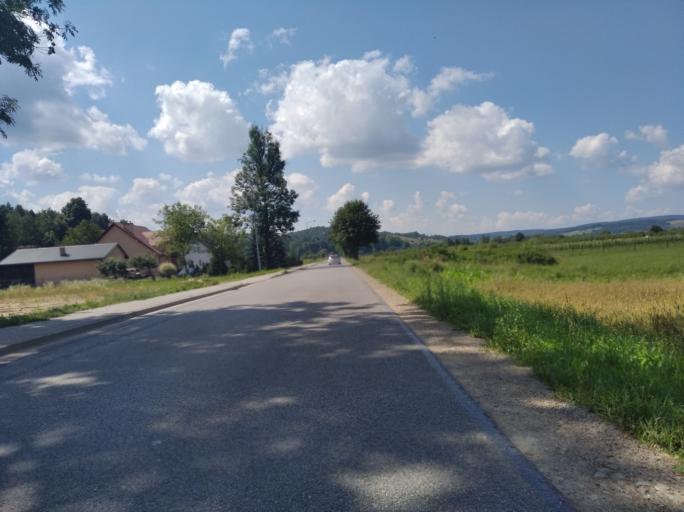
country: PL
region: Subcarpathian Voivodeship
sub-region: Powiat rzeszowski
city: Dynow
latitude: 49.7914
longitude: 22.2406
